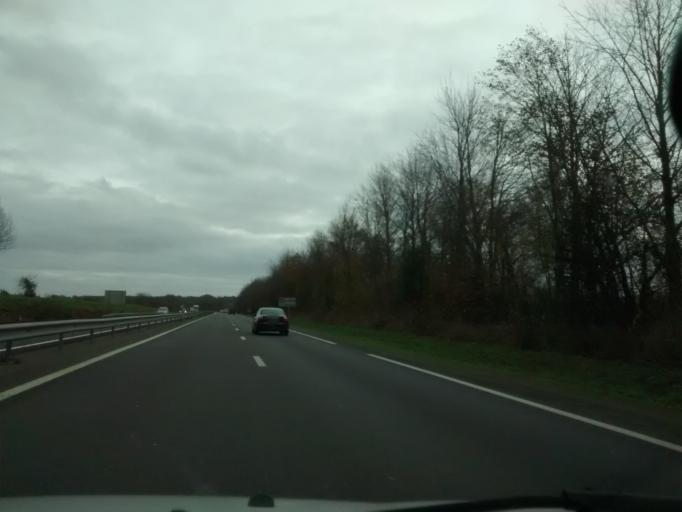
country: FR
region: Brittany
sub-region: Departement d'Ille-et-Vilaine
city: Tinteniac
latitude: 48.3066
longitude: -1.8329
